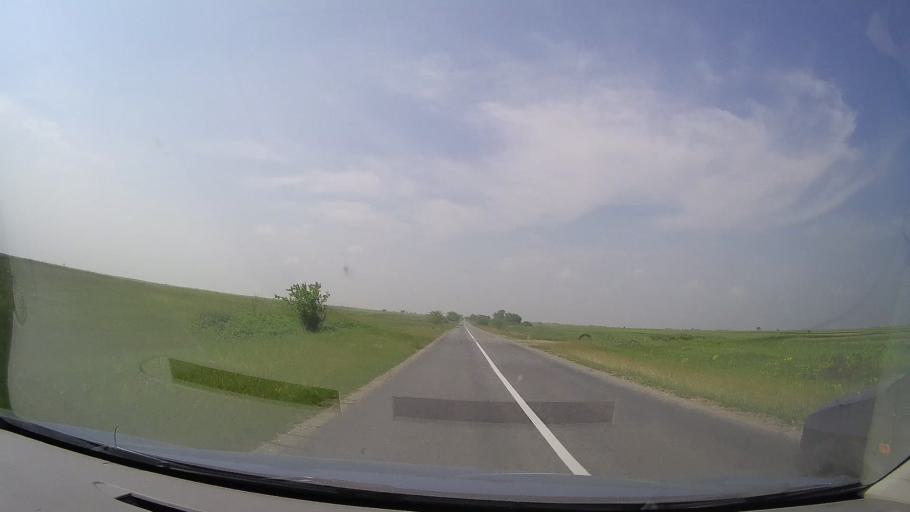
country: RS
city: Padina
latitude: 45.1602
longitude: 20.7499
